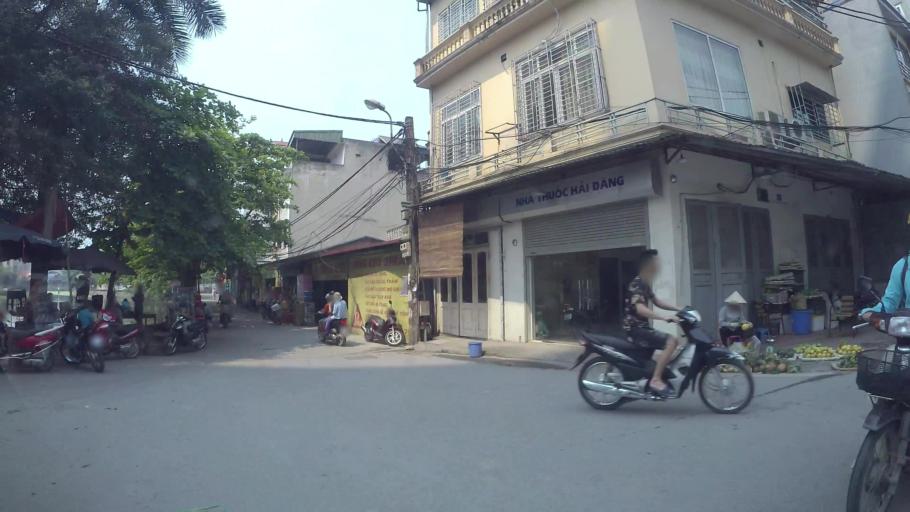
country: VN
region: Ha Noi
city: Van Dien
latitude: 20.9628
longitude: 105.8223
